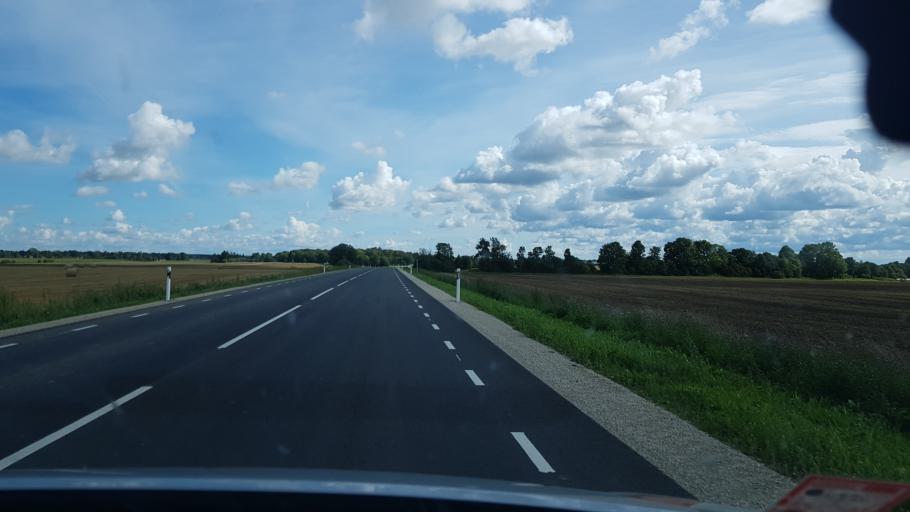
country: EE
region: Jaervamaa
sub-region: Paide linn
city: Paide
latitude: 58.8960
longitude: 25.7222
